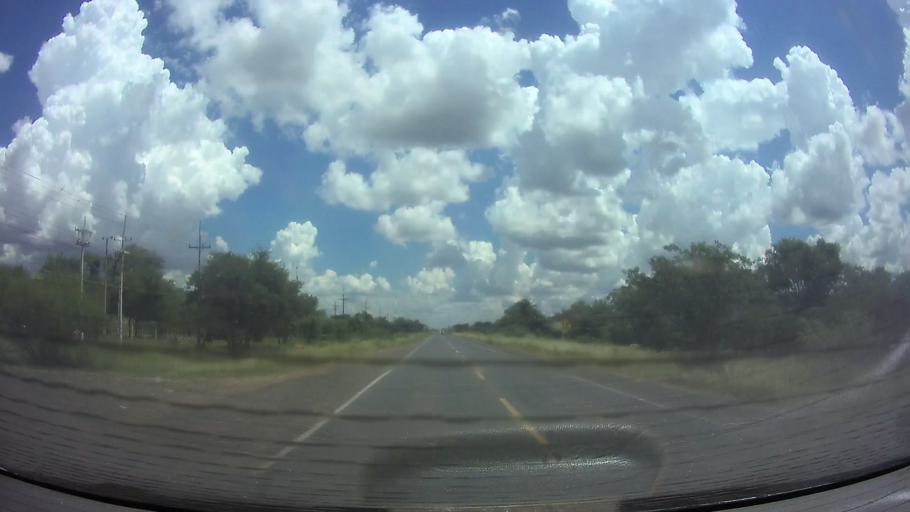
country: PY
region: Central
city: Colonia Mariano Roque Alonso
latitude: -25.1825
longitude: -57.5901
